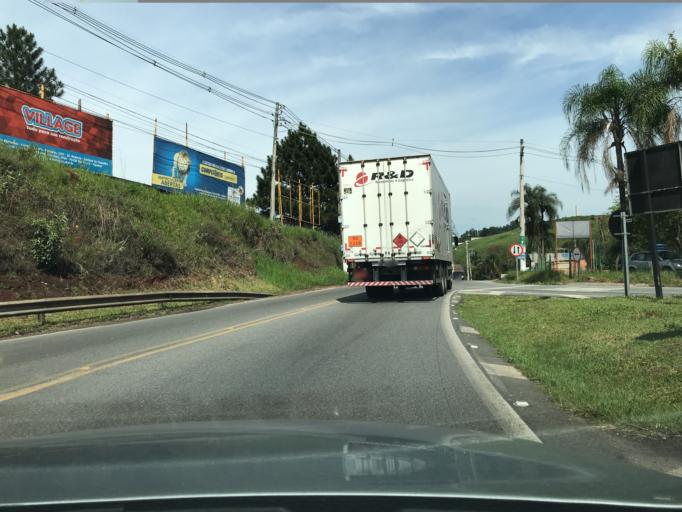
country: BR
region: Sao Paulo
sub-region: Cajamar
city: Cajamar
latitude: -23.4090
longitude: -46.8215
